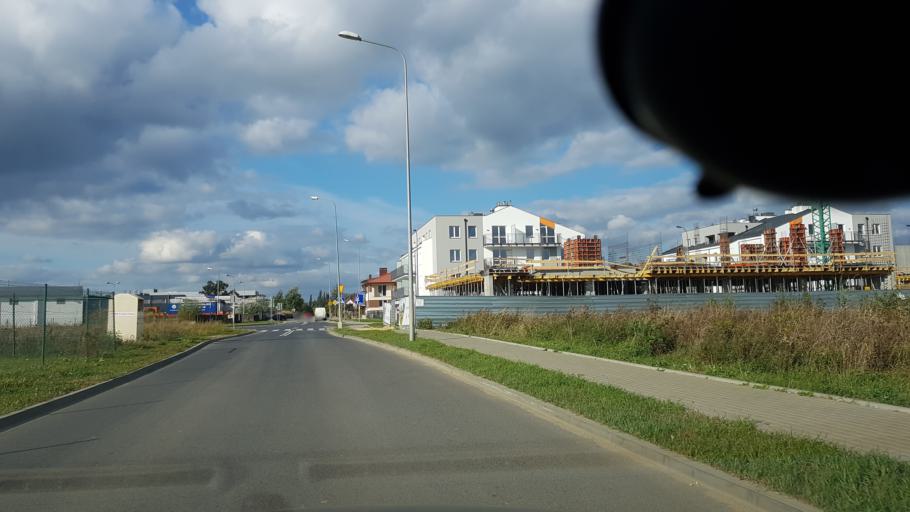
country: PL
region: Masovian Voivodeship
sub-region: Warszawa
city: Targowek
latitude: 52.3113
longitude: 21.0235
